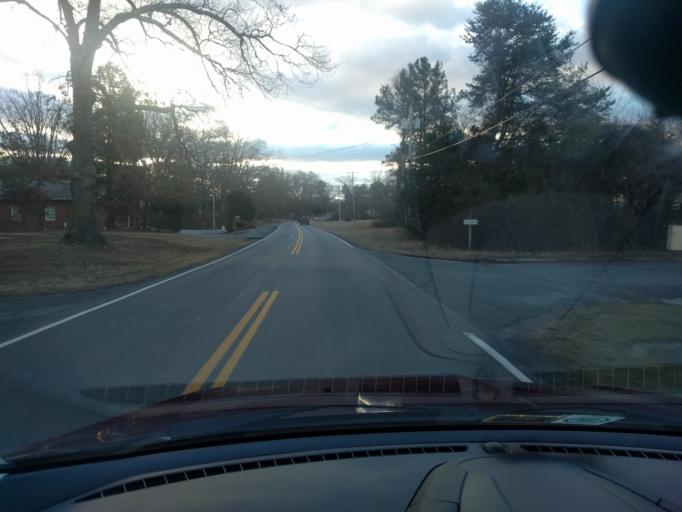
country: US
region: Virginia
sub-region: City of Bedford
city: Bedford
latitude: 37.3778
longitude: -79.5485
